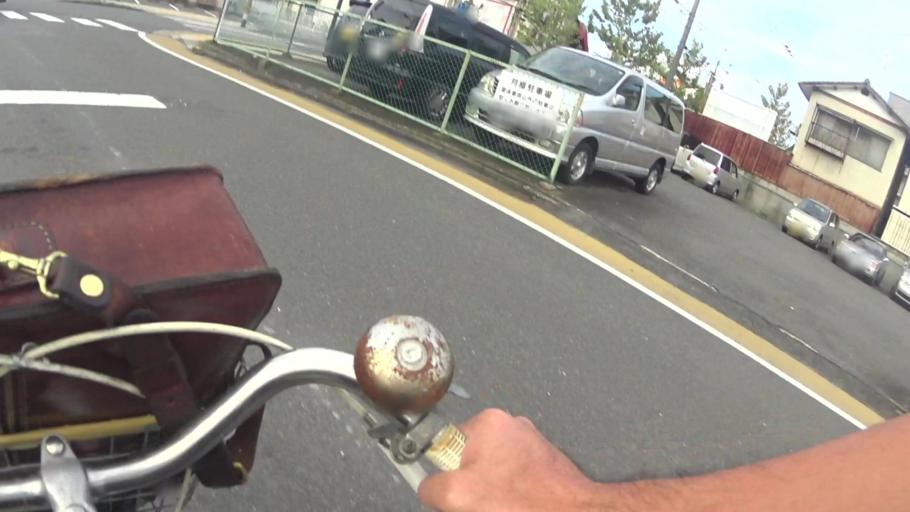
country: JP
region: Kyoto
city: Muko
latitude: 34.9320
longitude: 135.7095
